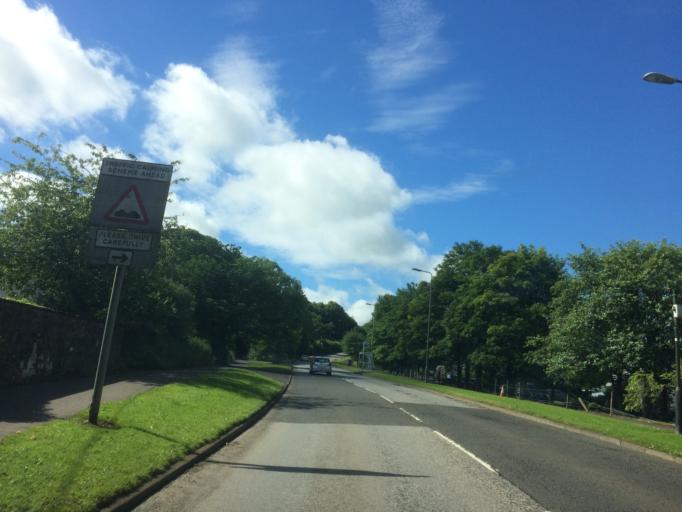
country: GB
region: Scotland
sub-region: East Renfrewshire
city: Newton Mearns
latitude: 55.7782
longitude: -4.3316
